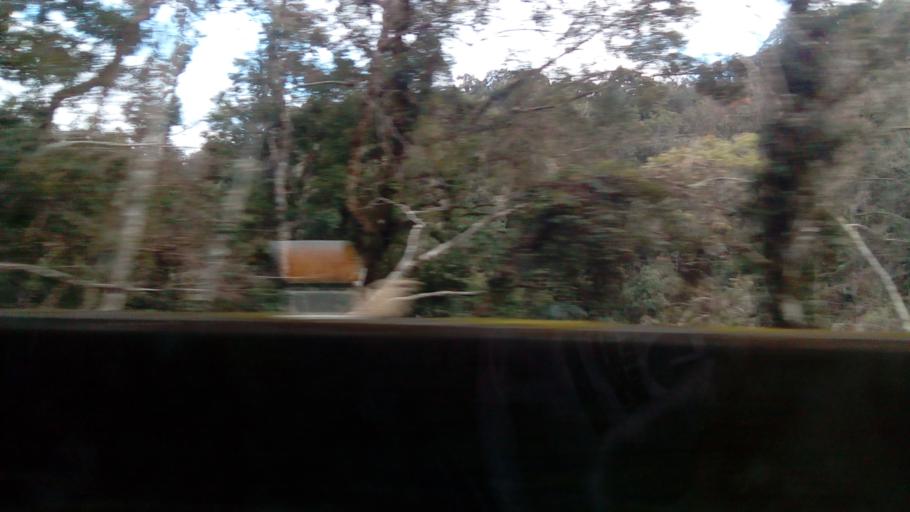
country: TW
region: Taiwan
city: Daxi
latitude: 24.4048
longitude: 121.3644
